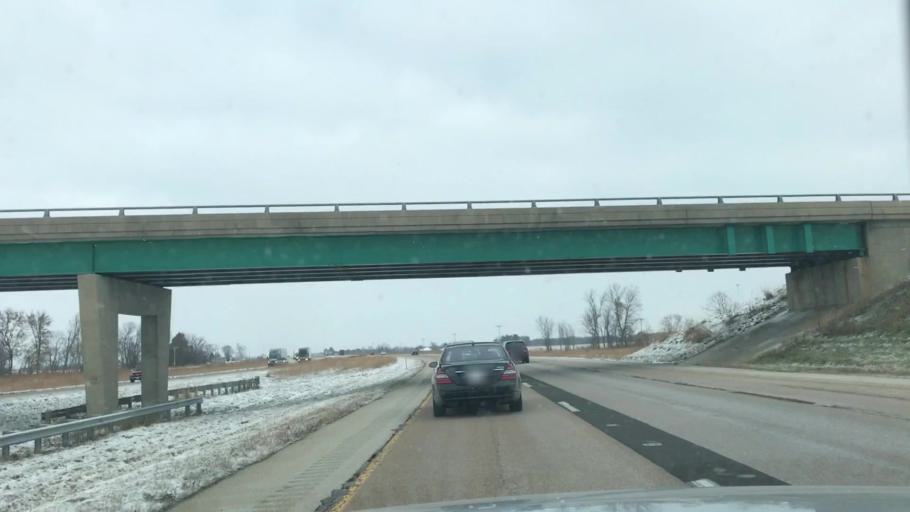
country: US
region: Illinois
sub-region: Montgomery County
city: Litchfield
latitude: 39.2337
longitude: -89.6415
